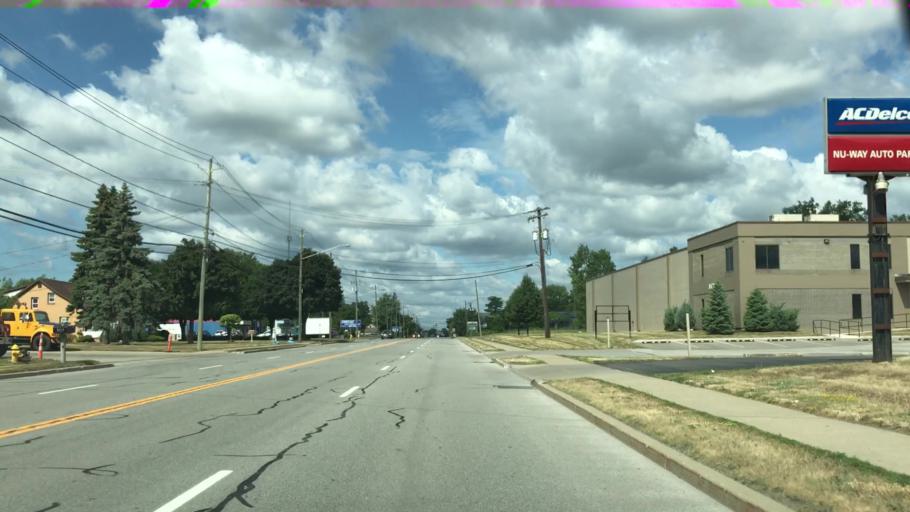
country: US
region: New York
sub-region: Erie County
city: Cheektowaga
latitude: 42.9040
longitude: -78.7430
